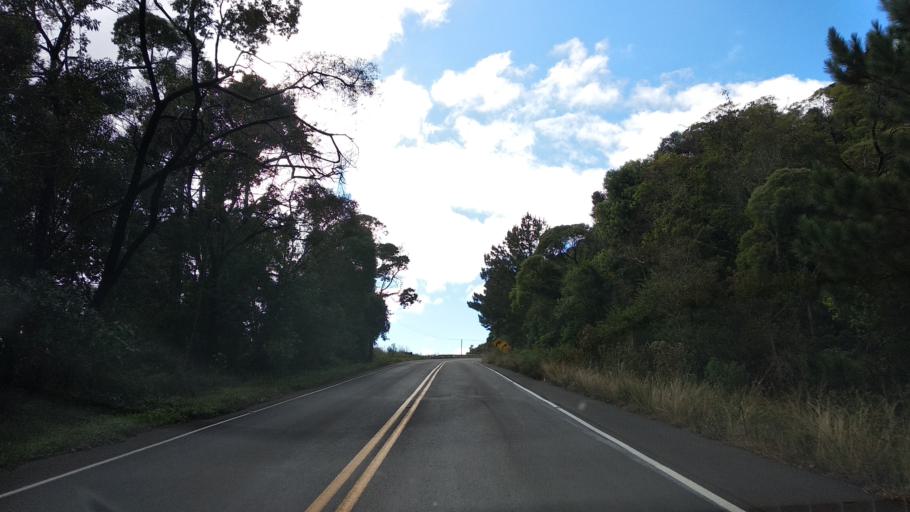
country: BR
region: Santa Catarina
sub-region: Lages
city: Lages
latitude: -27.8677
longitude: -50.1851
